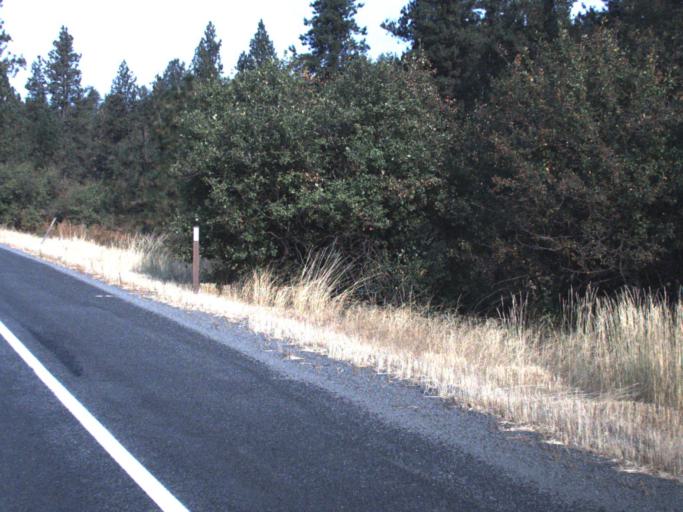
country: US
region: Washington
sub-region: Spokane County
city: Veradale
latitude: 47.4444
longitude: -117.1161
